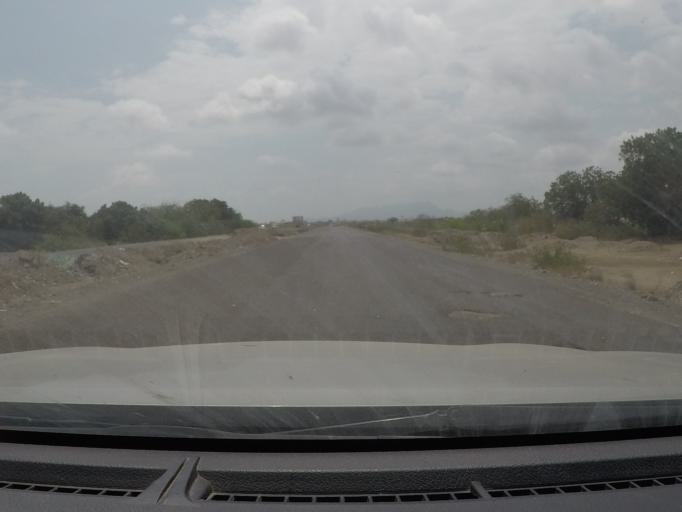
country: YE
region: Aden
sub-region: Ash Shaikh Outhman
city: Ash Shaykh `Uthman
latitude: 12.9144
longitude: 45.0092
